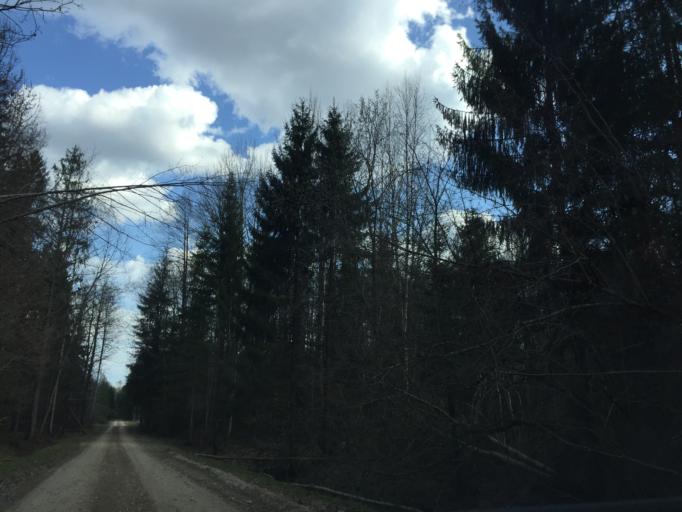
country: LV
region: Skriveri
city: Skriveri
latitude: 56.7978
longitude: 25.2149
